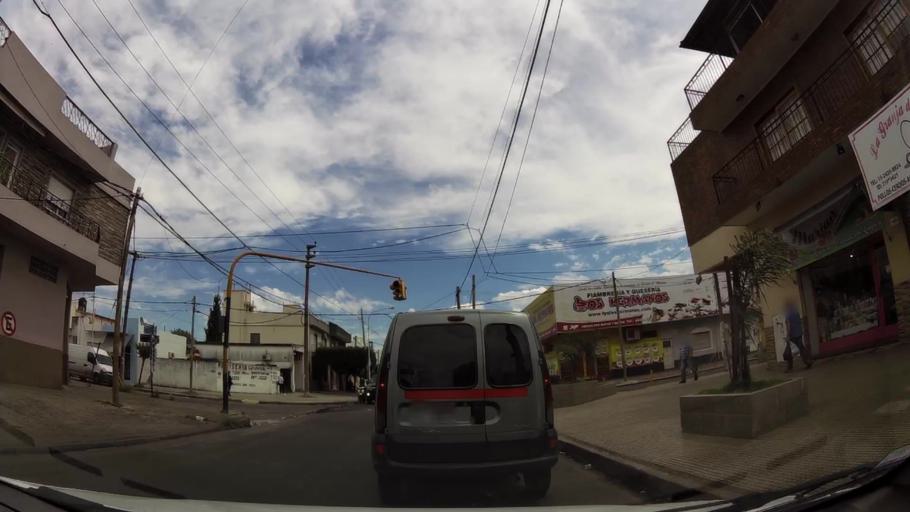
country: AR
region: Buenos Aires
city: San Justo
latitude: -34.6832
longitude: -58.5262
